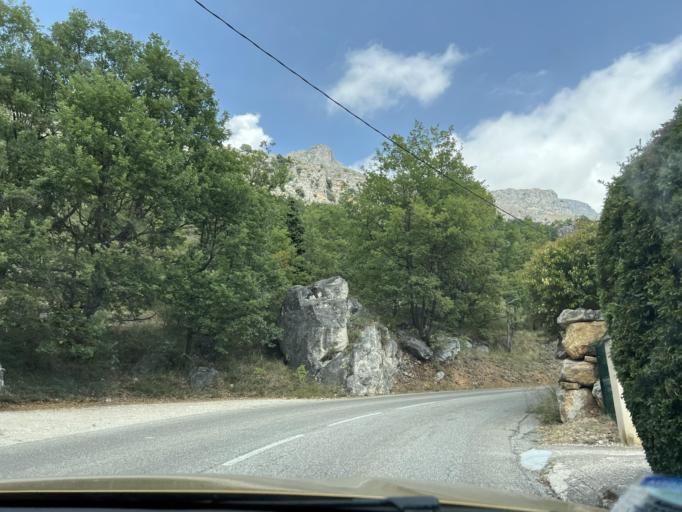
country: FR
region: Provence-Alpes-Cote d'Azur
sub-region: Departement des Alpes-Maritimes
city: Grasse
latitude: 43.7975
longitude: 6.9385
